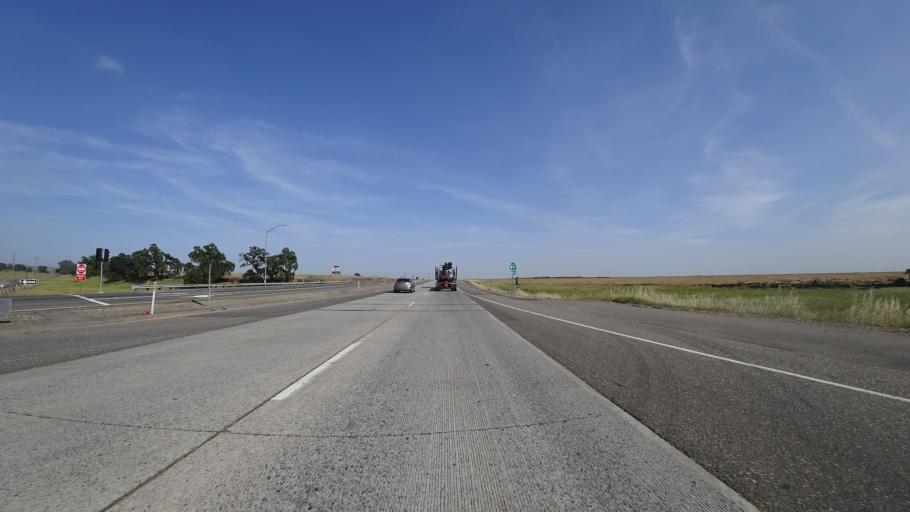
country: US
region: California
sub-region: Butte County
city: Durham
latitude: 39.6657
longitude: -121.7440
